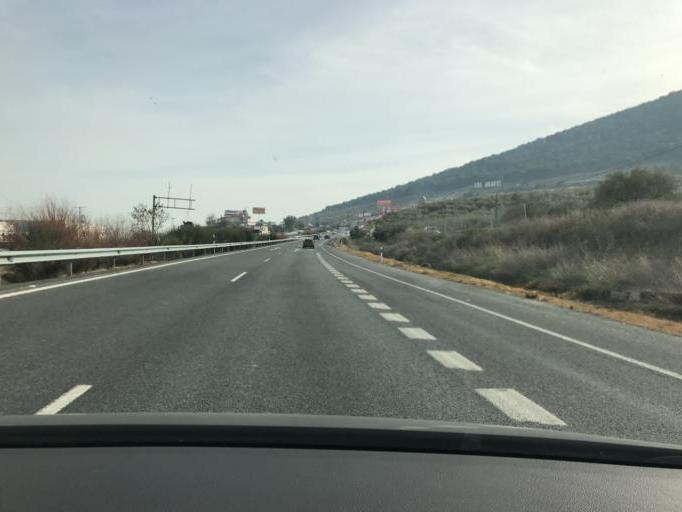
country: ES
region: Andalusia
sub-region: Provincia de Granada
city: Loja
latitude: 37.1665
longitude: -4.1751
